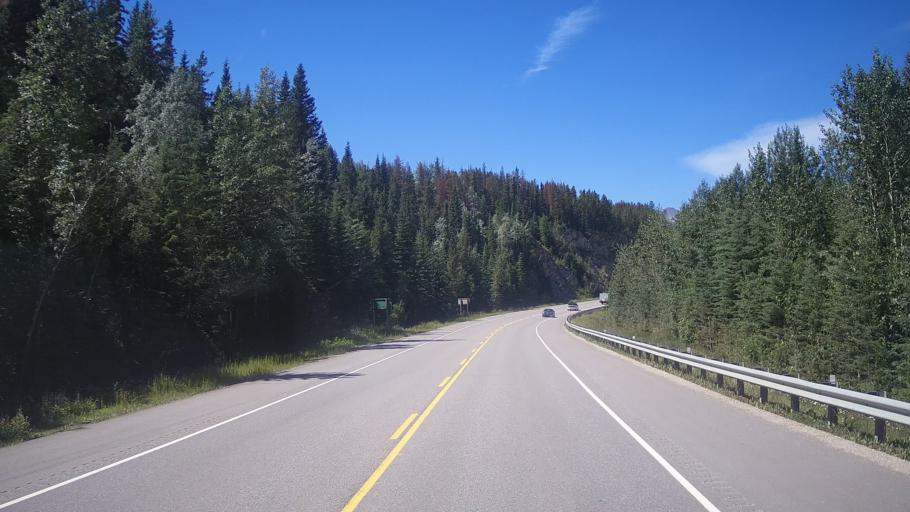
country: CA
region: Alberta
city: Jasper Park Lodge
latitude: 52.8823
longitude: -118.4323
